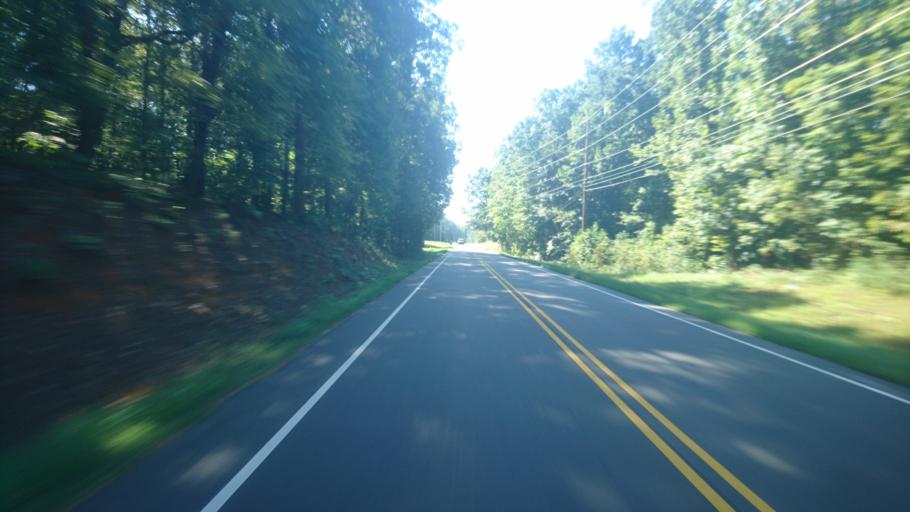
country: US
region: North Carolina
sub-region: Orange County
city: Hillsborough
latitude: 36.0109
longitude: -79.0694
